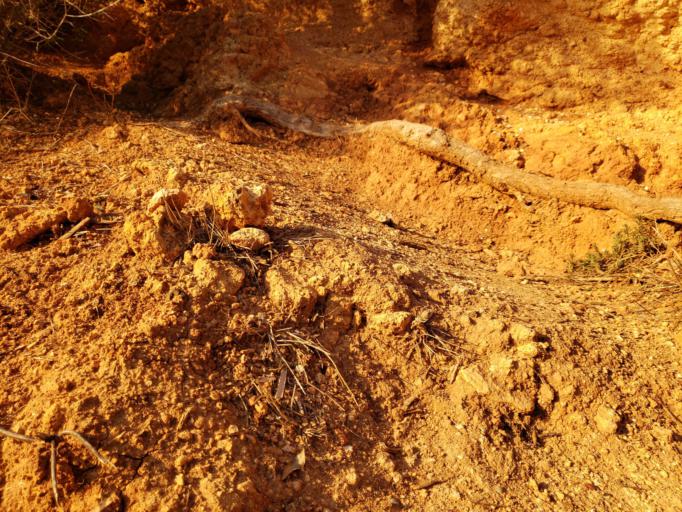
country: PT
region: Faro
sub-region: Portimao
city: Alvor
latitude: 37.1333
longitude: -8.5951
